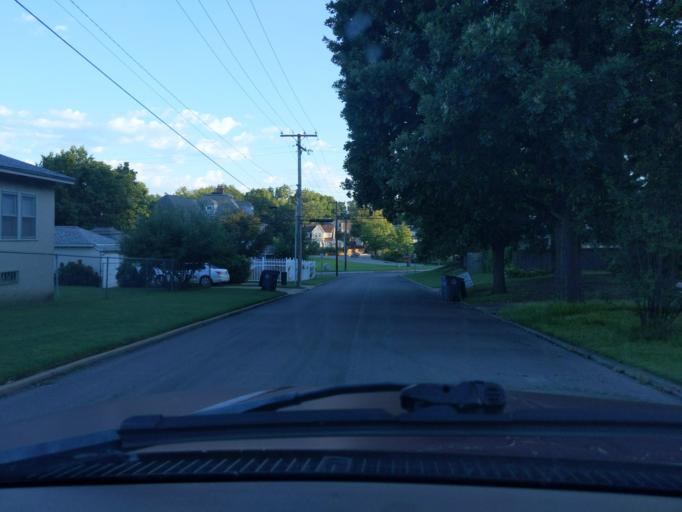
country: US
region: Oklahoma
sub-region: Tulsa County
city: Tulsa
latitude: 36.1343
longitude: -95.9704
